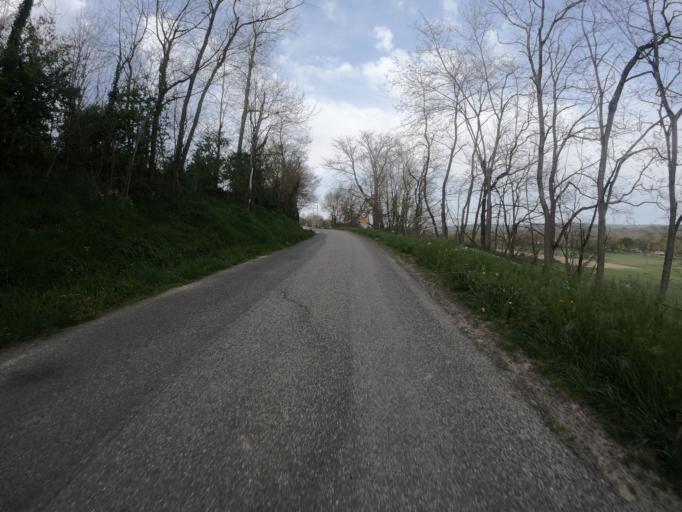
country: FR
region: Midi-Pyrenees
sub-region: Departement de l'Ariege
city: La Tour-du-Crieu
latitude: 43.1379
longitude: 1.7124
